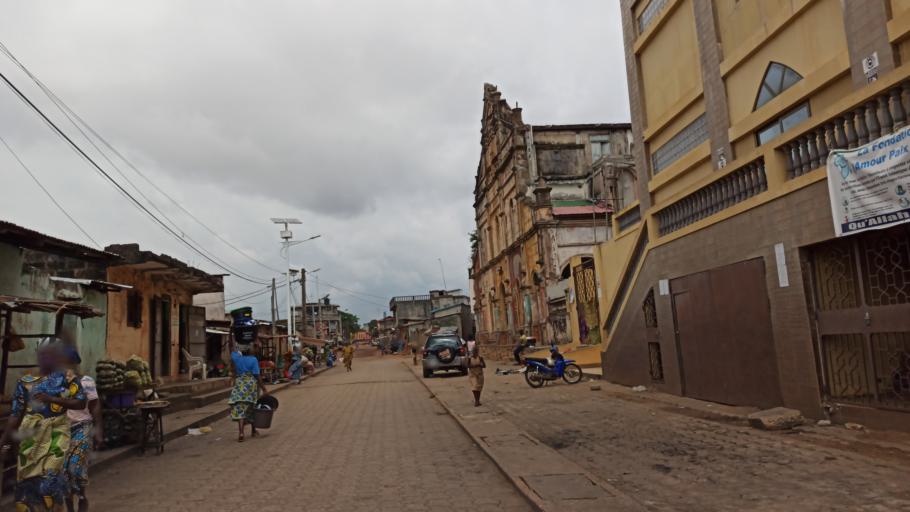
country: BJ
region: Queme
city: Porto-Novo
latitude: 6.4714
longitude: 2.6278
